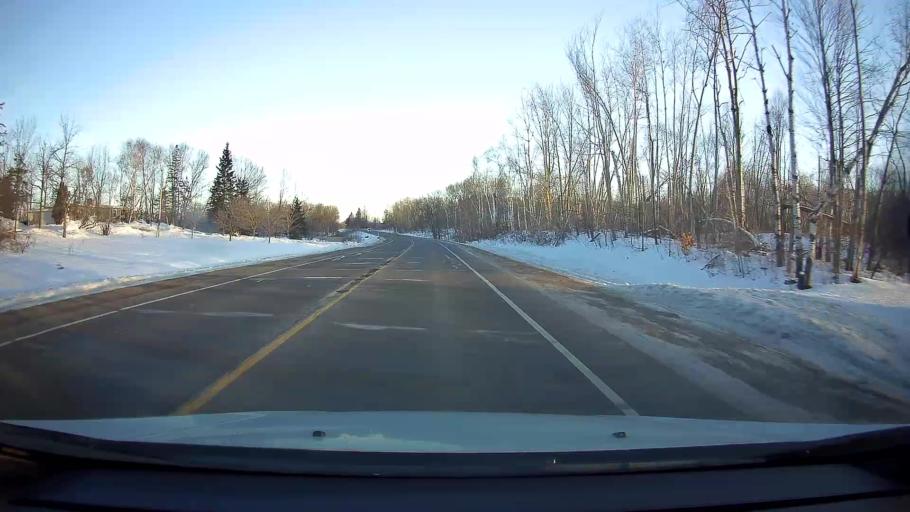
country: US
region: Wisconsin
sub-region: Barron County
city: Turtle Lake
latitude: 45.4188
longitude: -92.1310
